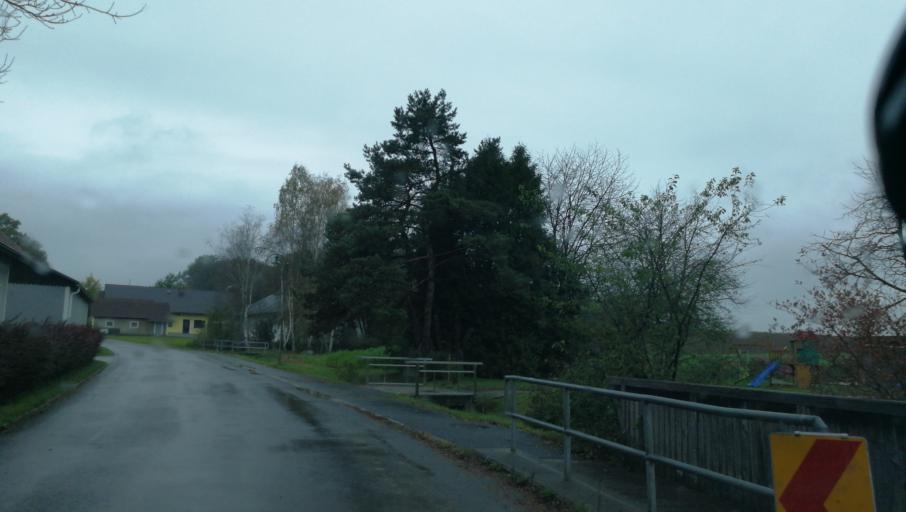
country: AT
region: Styria
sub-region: Politischer Bezirk Leibnitz
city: Strass in Steiermark
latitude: 46.7354
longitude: 15.6601
